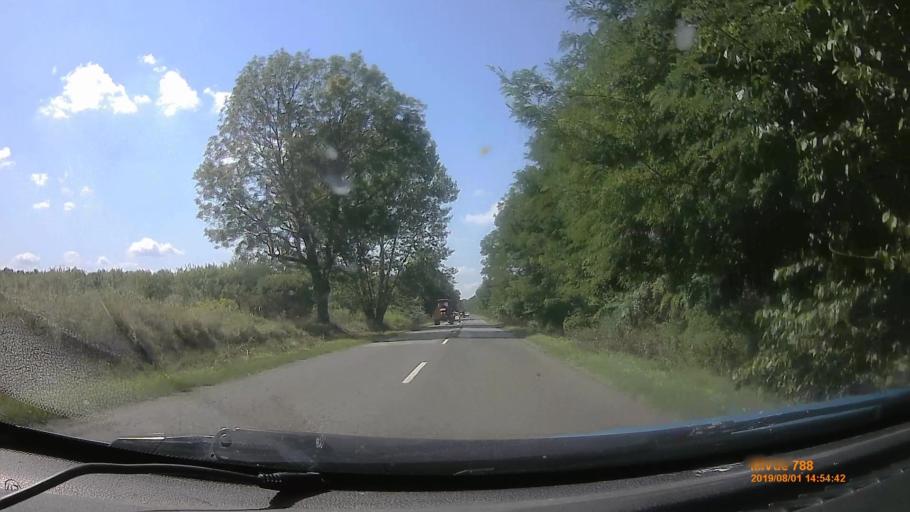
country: HU
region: Baranya
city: Vajszlo
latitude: 45.8663
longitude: 17.9666
